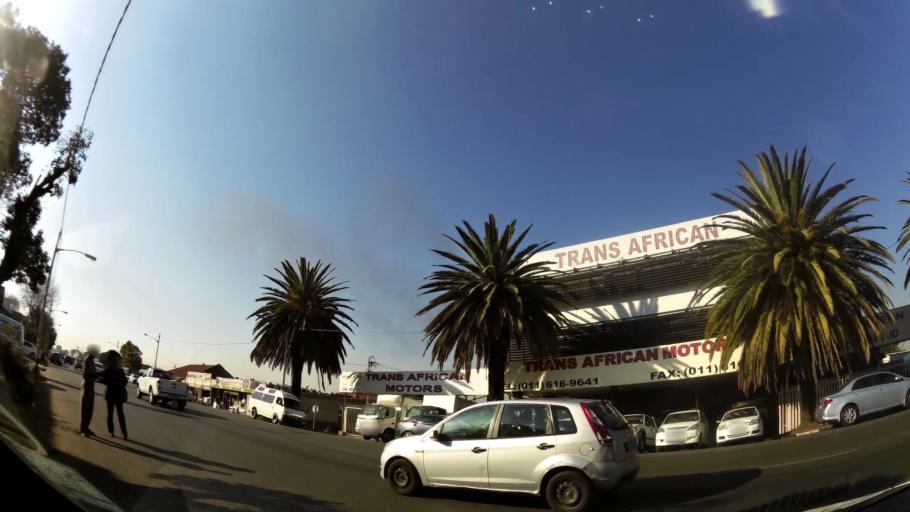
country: ZA
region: Gauteng
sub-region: City of Johannesburg Metropolitan Municipality
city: Johannesburg
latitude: -26.2020
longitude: 28.1093
